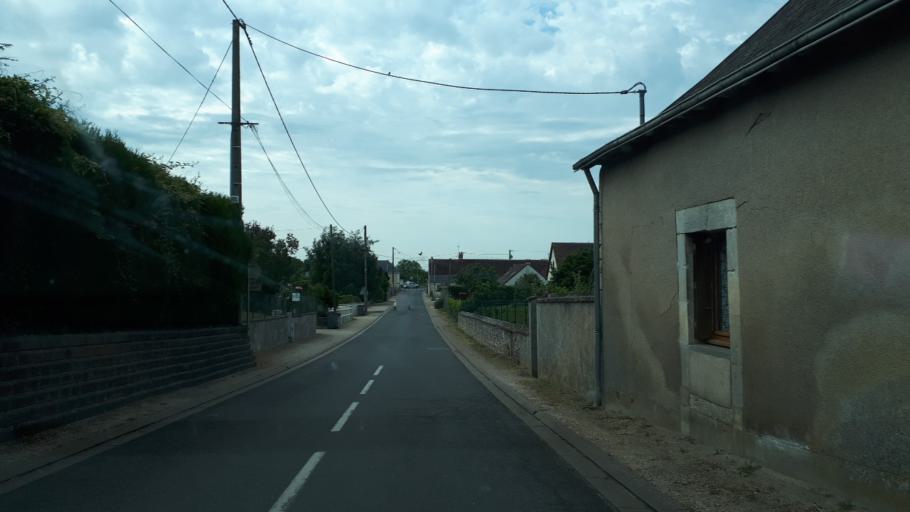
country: FR
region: Centre
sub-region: Departement du Loir-et-Cher
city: Villiers-sur-Loir
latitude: 47.7496
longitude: 0.9879
